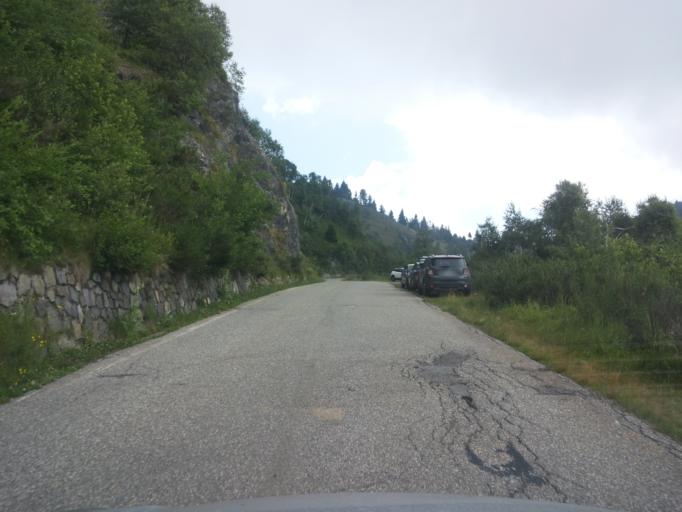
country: IT
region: Piedmont
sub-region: Provincia di Biella
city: Sagliano Micca
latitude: 45.6613
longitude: 8.0577
